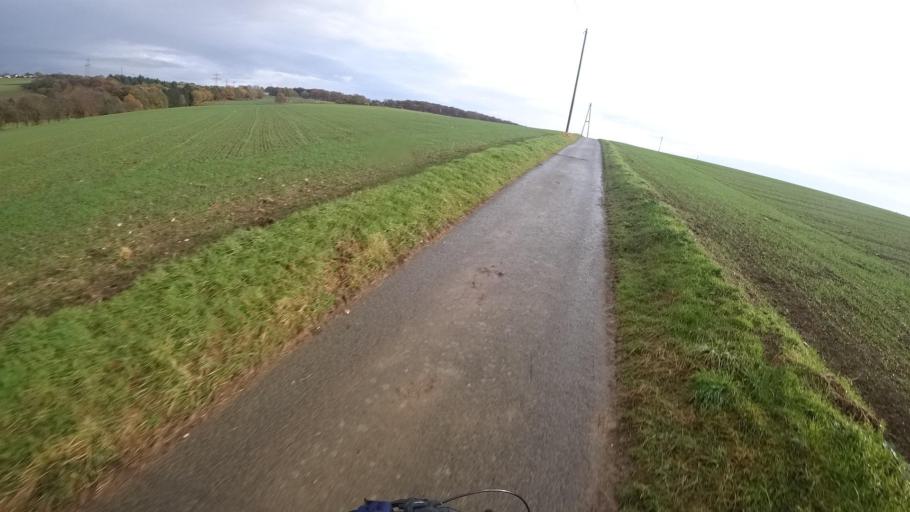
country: DE
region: Rheinland-Pfalz
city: Ney
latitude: 50.1801
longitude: 7.5201
